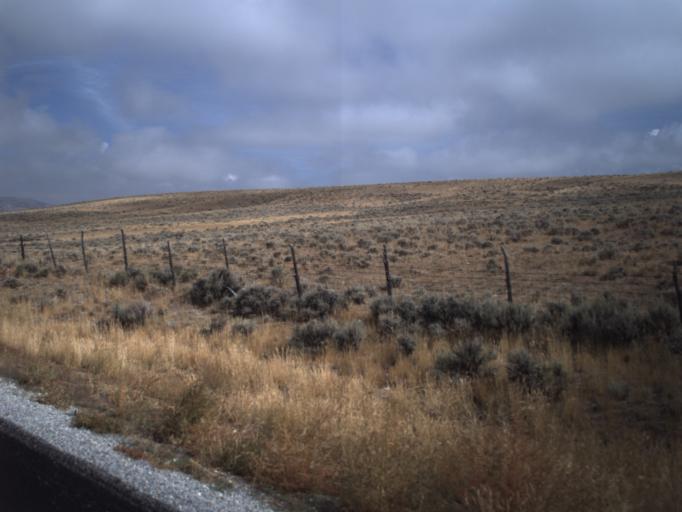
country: US
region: Utah
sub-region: Rich County
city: Randolph
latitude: 41.4825
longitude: -111.1161
